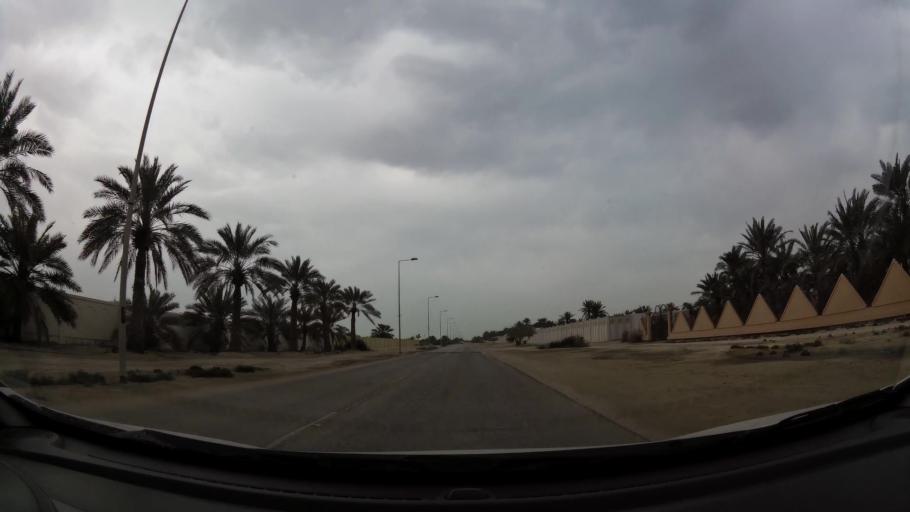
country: BH
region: Central Governorate
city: Dar Kulayb
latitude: 26.0364
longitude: 50.4861
